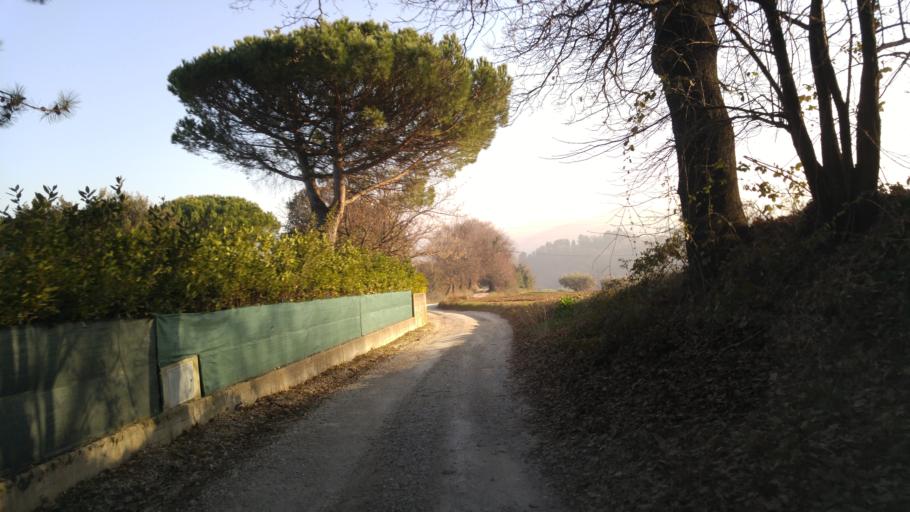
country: IT
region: The Marches
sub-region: Provincia di Pesaro e Urbino
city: Fenile
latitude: 43.8528
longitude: 12.9631
